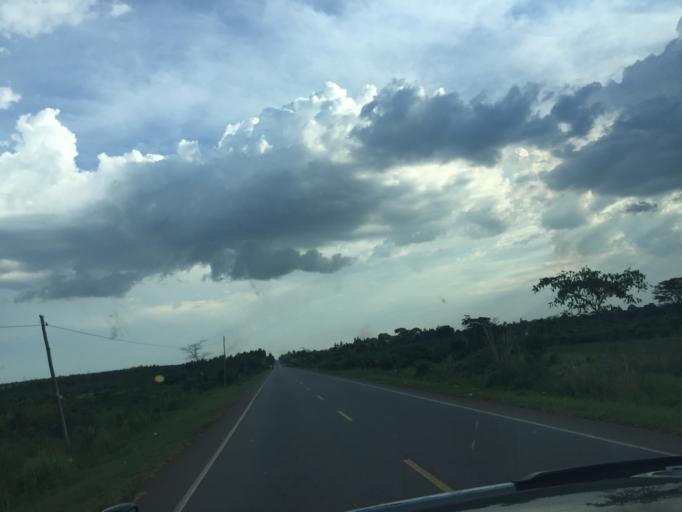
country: UG
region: Central Region
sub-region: Nakasongola District
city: Nakasongola
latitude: 1.0792
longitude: 32.4665
